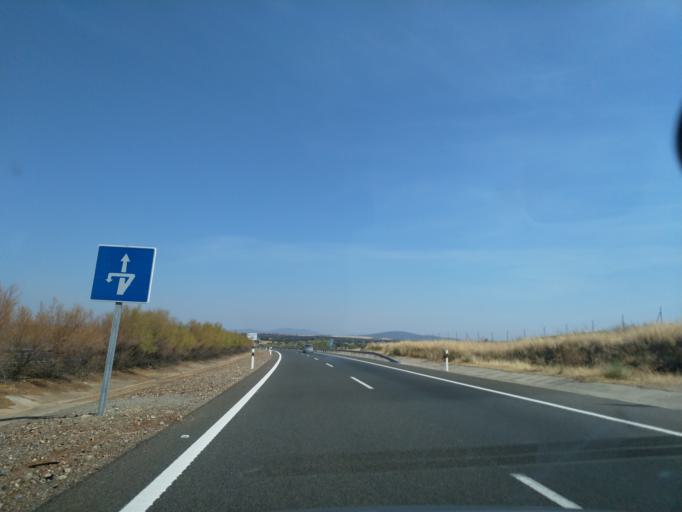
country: ES
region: Extremadura
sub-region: Provincia de Badajoz
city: Merida
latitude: 38.9691
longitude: -6.3362
